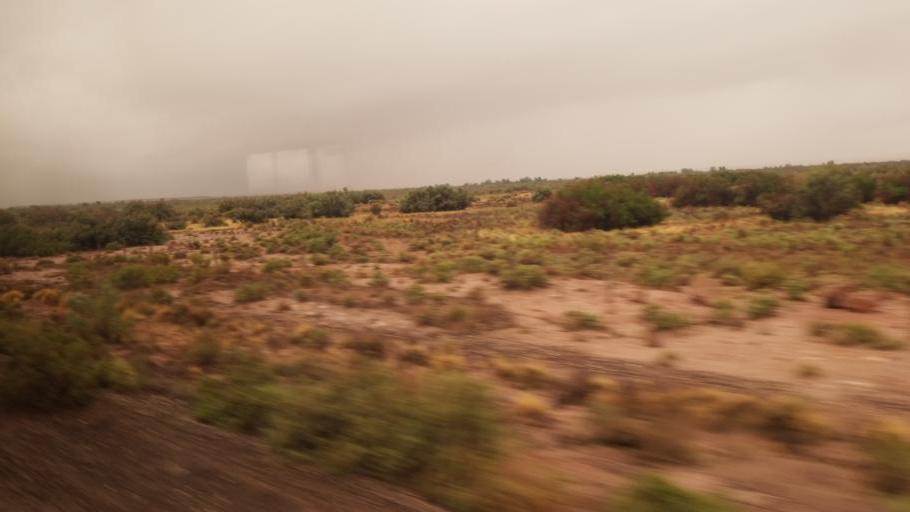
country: US
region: Arizona
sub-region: Navajo County
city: Joseph City
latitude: 34.9674
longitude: -110.4511
